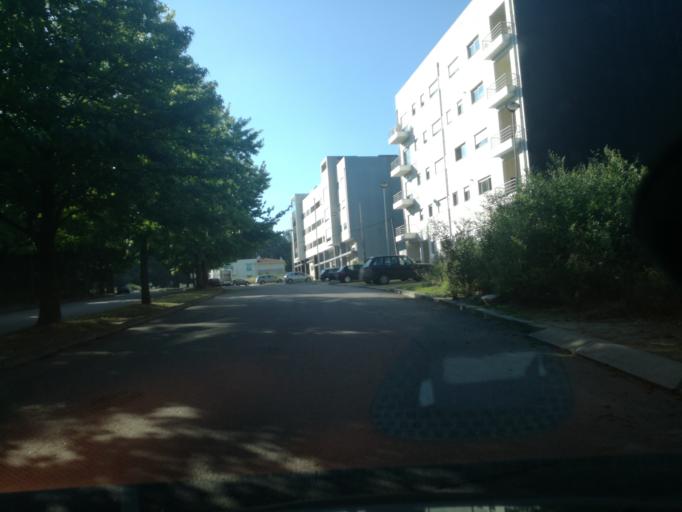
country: PT
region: Porto
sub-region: Maia
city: Gemunde
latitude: 41.2494
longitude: -8.6547
